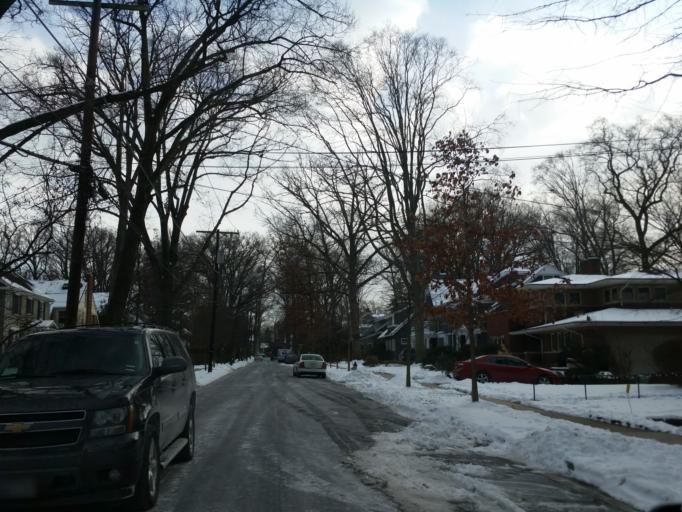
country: US
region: Maryland
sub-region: Montgomery County
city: Chevy Chase
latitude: 38.9812
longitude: -77.0832
